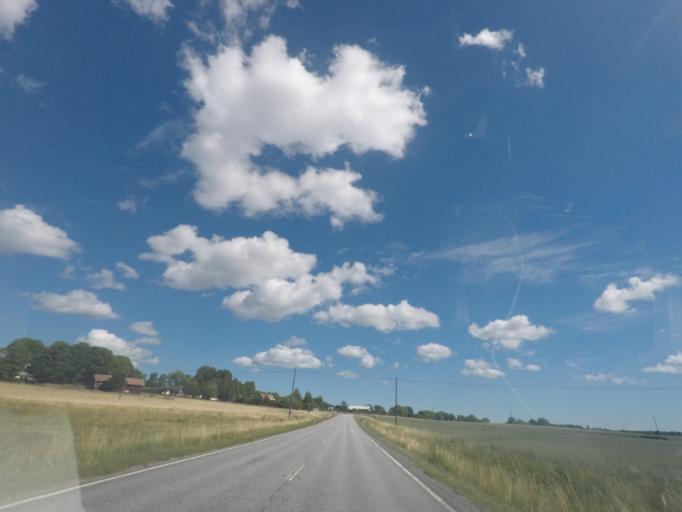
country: SE
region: Stockholm
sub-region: Norrtalje Kommun
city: Hallstavik
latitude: 59.9549
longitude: 18.7817
